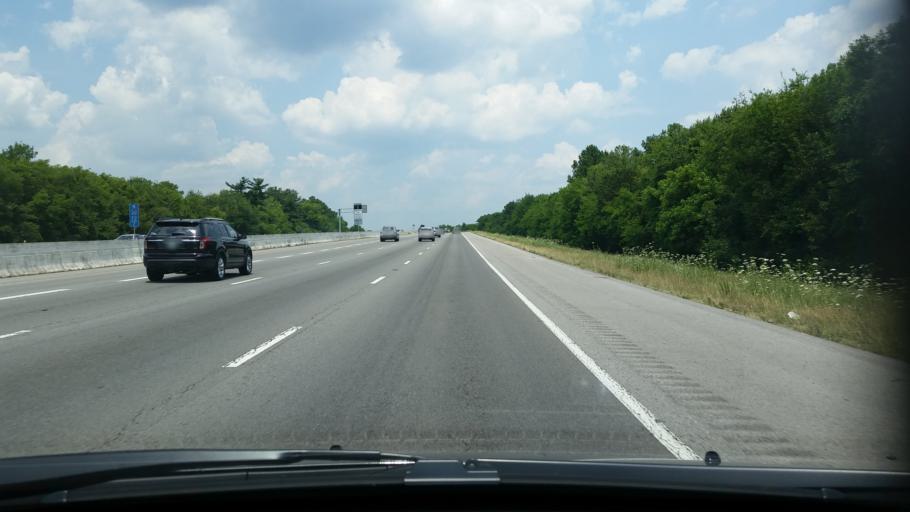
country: US
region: Tennessee
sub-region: Williamson County
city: Brentwood Estates
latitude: 36.0060
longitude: -86.7889
